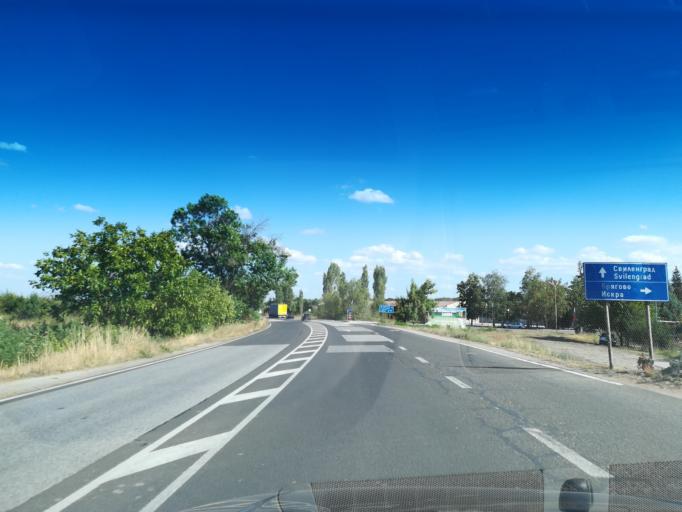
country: BG
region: Stara Zagora
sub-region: Obshtina Chirpan
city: Chirpan
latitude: 42.0727
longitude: 25.1986
